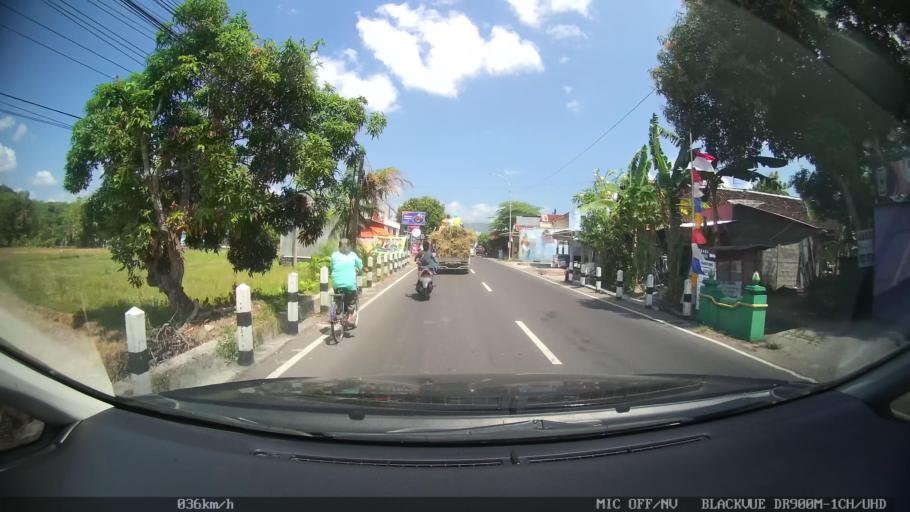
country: ID
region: Daerah Istimewa Yogyakarta
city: Sewon
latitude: -7.9131
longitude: 110.3825
